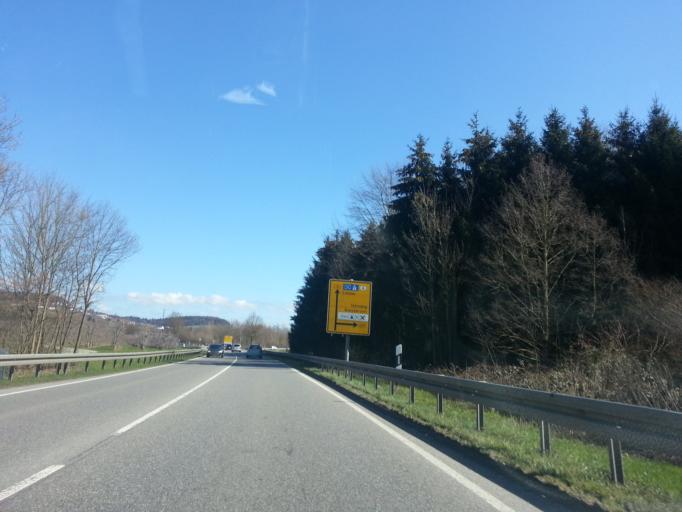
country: DE
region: Baden-Wuerttemberg
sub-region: Tuebingen Region
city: Kressbronn am Bodensee
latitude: 47.6081
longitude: 9.5806
